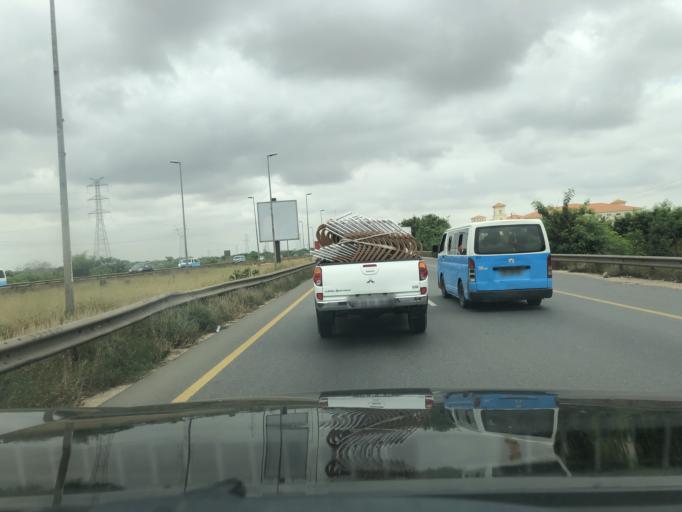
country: AO
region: Luanda
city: Luanda
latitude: -8.9729
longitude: 13.2739
